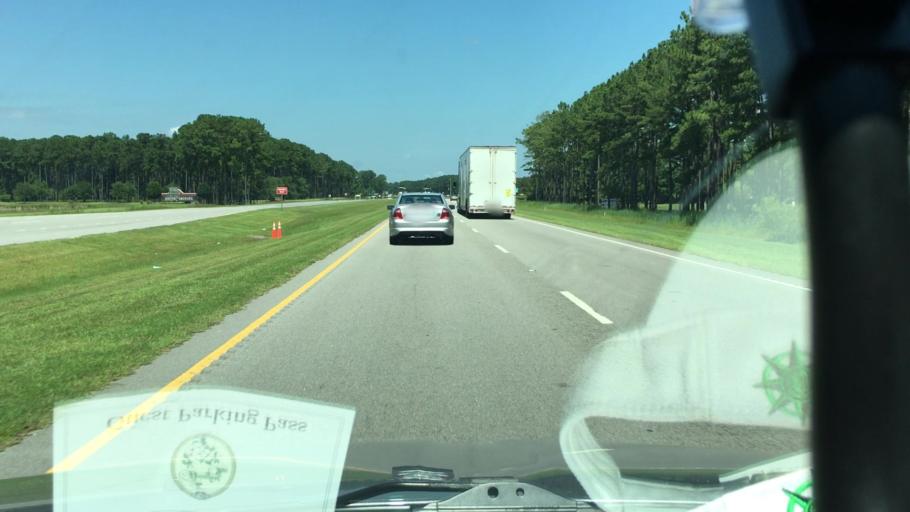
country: US
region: South Carolina
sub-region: Jasper County
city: Hardeeville
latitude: 32.3040
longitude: -80.9703
